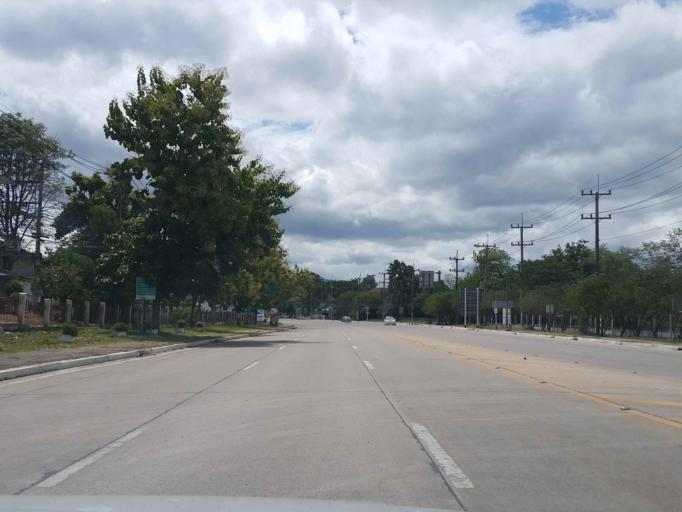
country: TH
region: Tak
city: Tak
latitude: 16.8856
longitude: 99.1256
